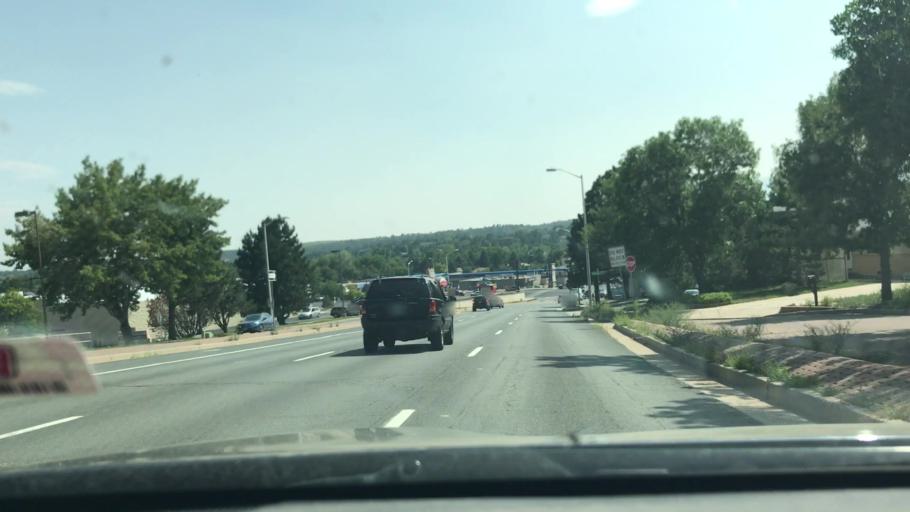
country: US
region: Colorado
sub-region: El Paso County
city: Colorado Springs
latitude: 38.9066
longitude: -104.7748
